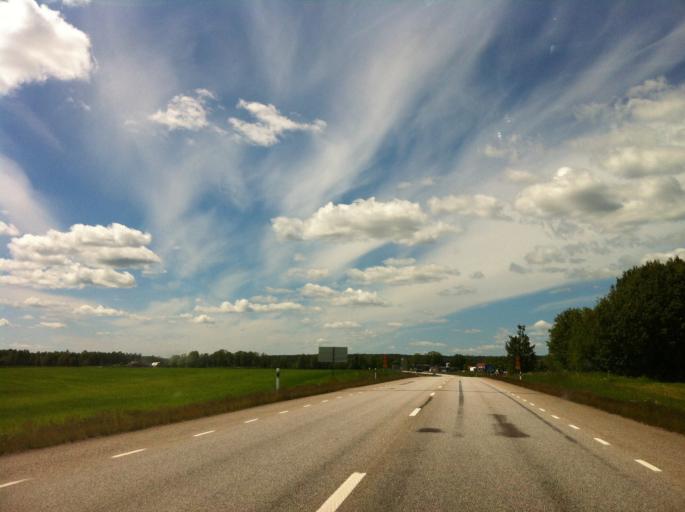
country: SE
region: Vaestra Goetaland
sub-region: Amals Kommun
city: Amal
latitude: 58.9795
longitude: 12.6402
